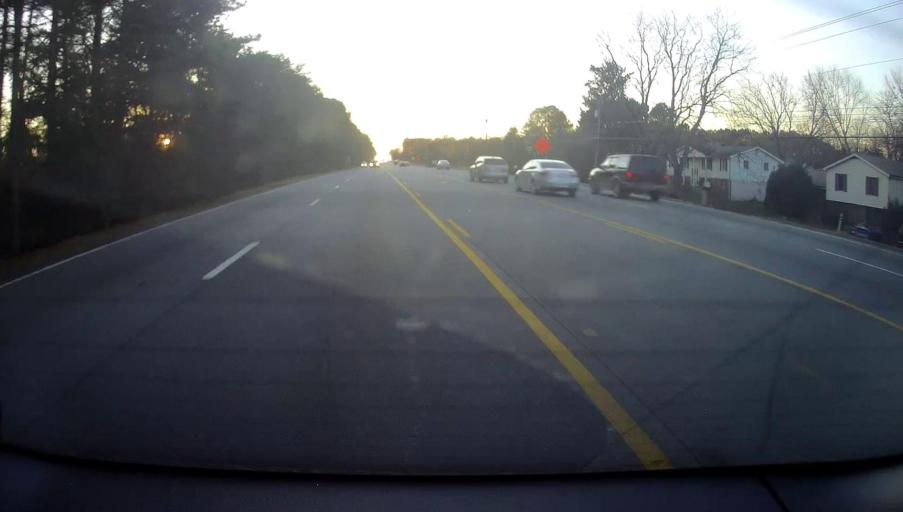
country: US
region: Georgia
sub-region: Clayton County
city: Riverdale
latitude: 33.5509
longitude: -84.4566
